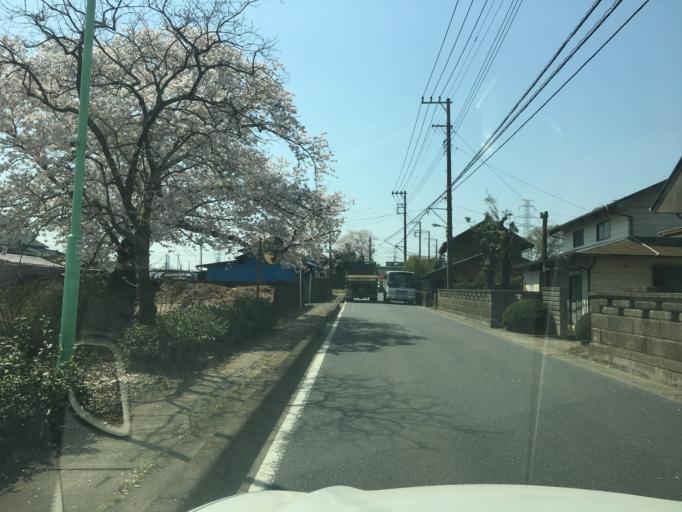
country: JP
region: Saitama
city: Sayama
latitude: 35.8504
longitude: 139.4515
